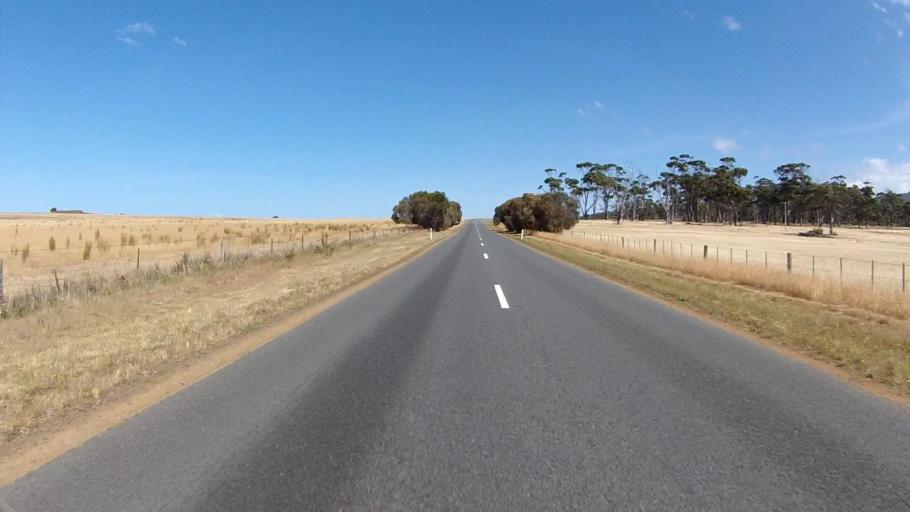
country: AU
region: Tasmania
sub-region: Sorell
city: Sorell
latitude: -42.2080
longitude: 148.0409
